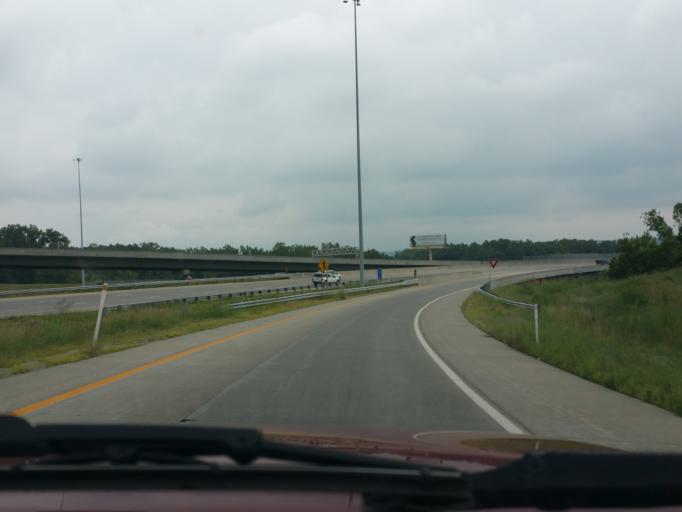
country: US
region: Kansas
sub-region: Wyandotte County
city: Kansas City
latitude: 39.1039
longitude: -94.6808
